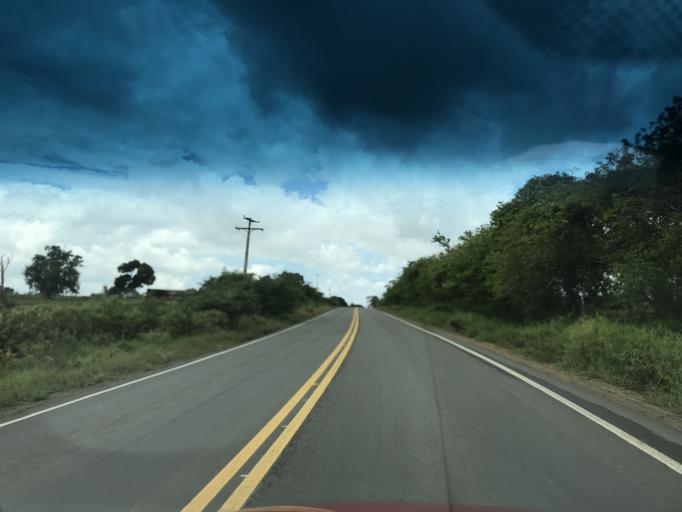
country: BR
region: Bahia
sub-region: Conceicao Do Almeida
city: Conceicao do Almeida
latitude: -12.7155
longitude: -39.2231
